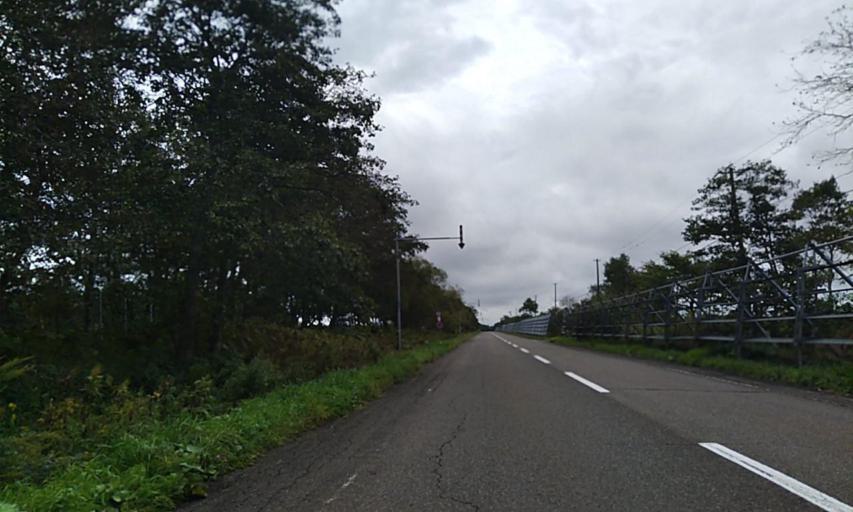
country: JP
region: Hokkaido
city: Nemuro
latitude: 43.3734
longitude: 145.2825
